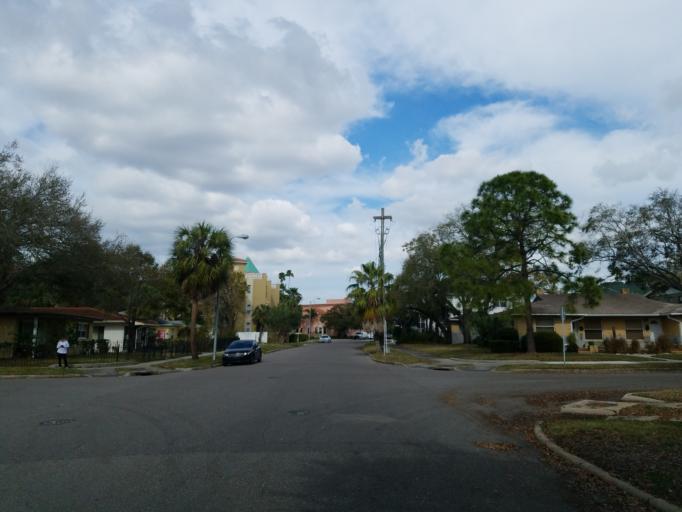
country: US
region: Florida
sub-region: Hillsborough County
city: Tampa
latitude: 27.9283
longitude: -82.4564
